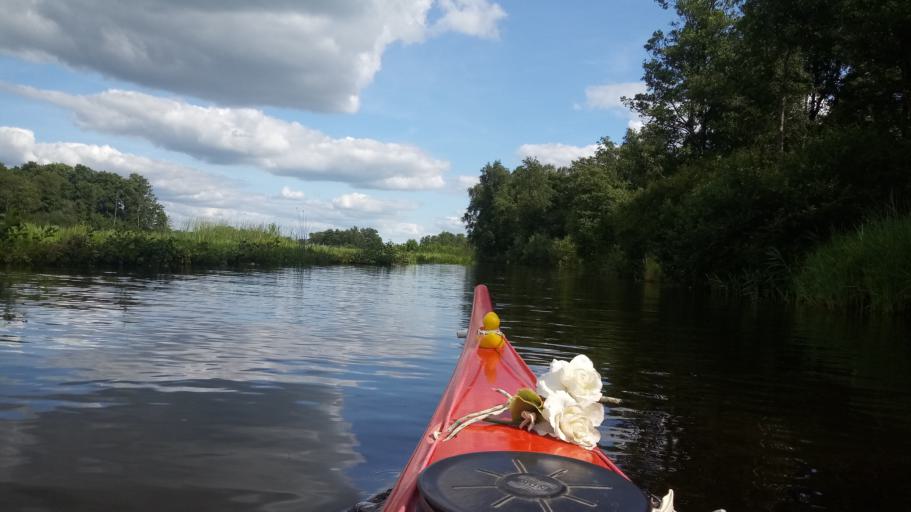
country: NL
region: Overijssel
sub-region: Gemeente Steenwijkerland
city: Wanneperveen
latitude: 52.7232
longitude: 6.1182
